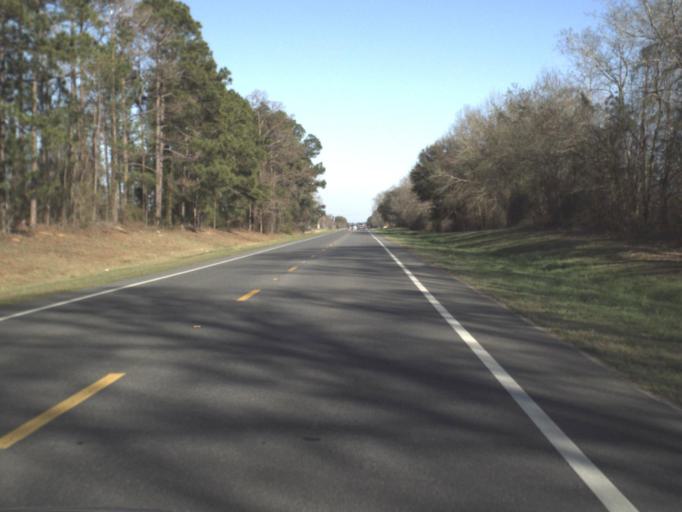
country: US
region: Florida
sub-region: Jackson County
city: Sneads
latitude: 30.7194
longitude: -85.0438
